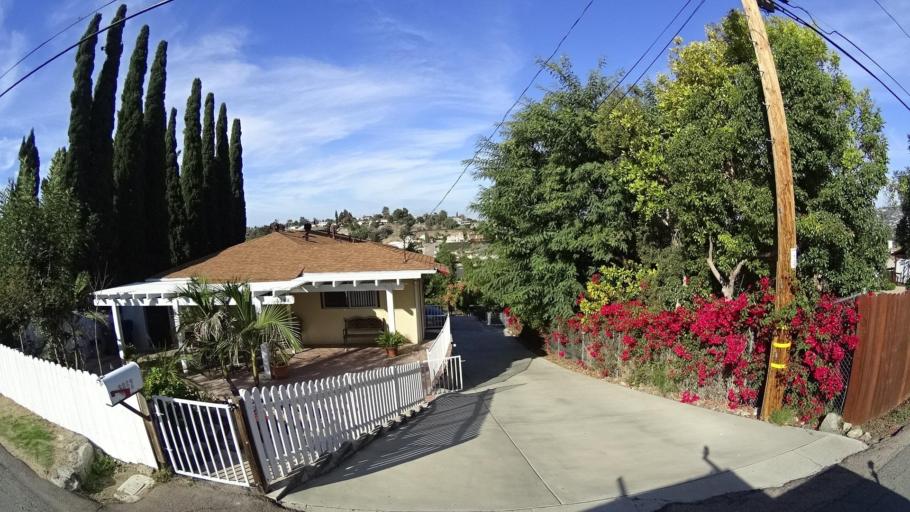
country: US
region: California
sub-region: San Diego County
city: Casa de Oro-Mount Helix
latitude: 32.7392
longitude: -116.9699
